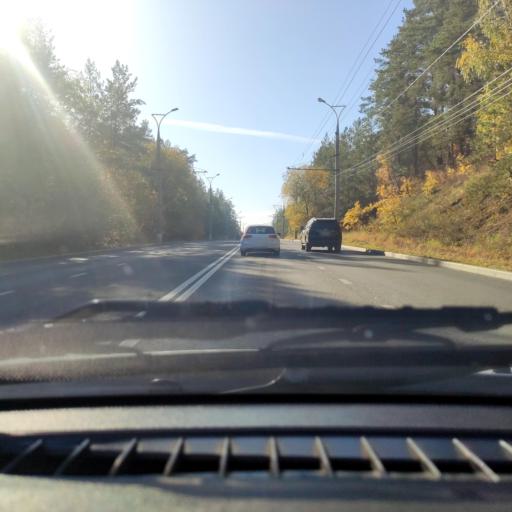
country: RU
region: Samara
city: Zhigulevsk
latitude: 53.4957
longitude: 49.4630
